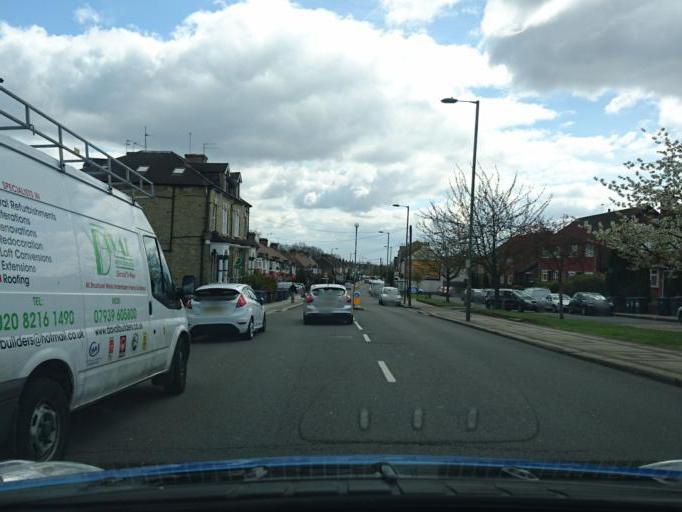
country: GB
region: England
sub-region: Greater London
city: Hadley Wood
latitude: 51.6251
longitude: -0.1573
